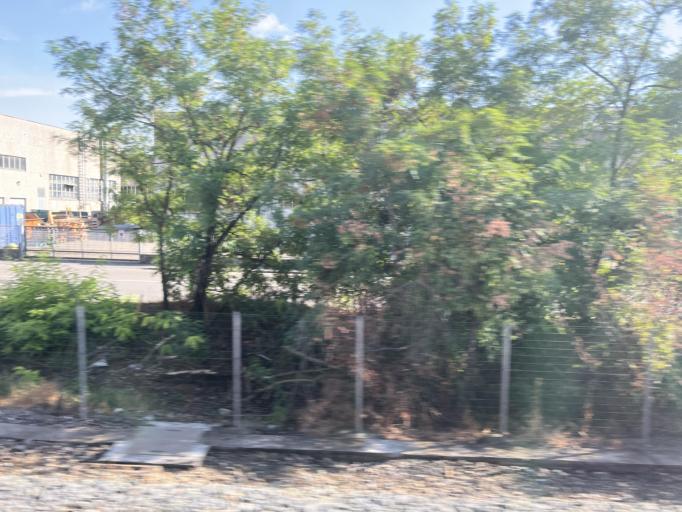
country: IT
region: Emilia-Romagna
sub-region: Provincia di Parma
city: Parma
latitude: 44.8146
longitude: 10.2967
